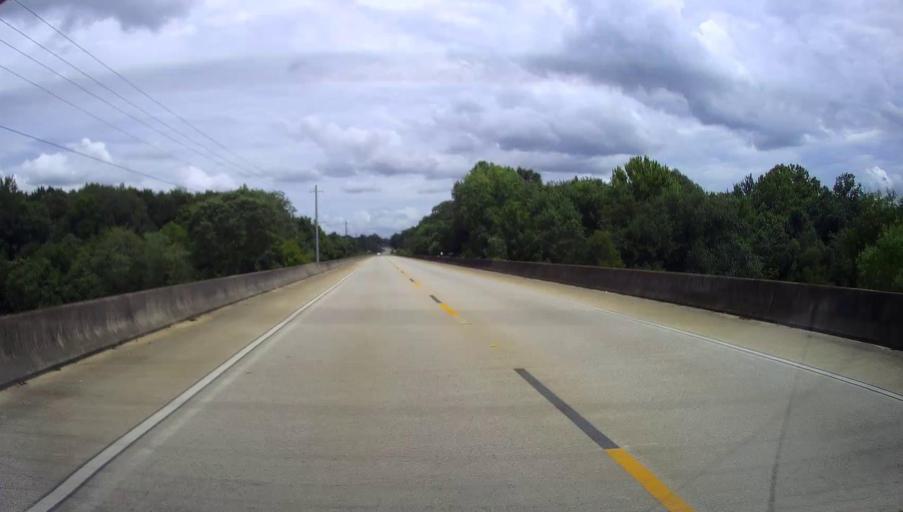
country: US
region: Georgia
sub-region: Macon County
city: Oglethorpe
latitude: 32.2929
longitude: -84.0442
